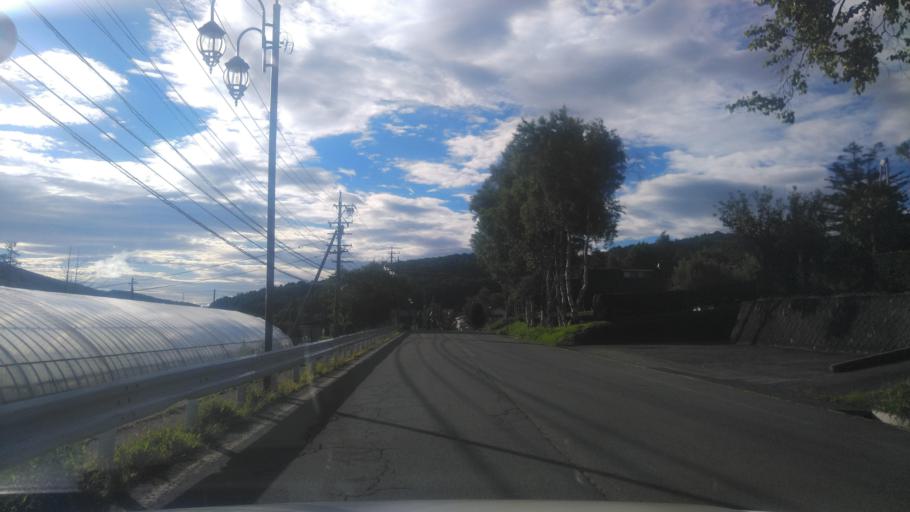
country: JP
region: Nagano
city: Suzaka
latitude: 36.5320
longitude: 138.3290
